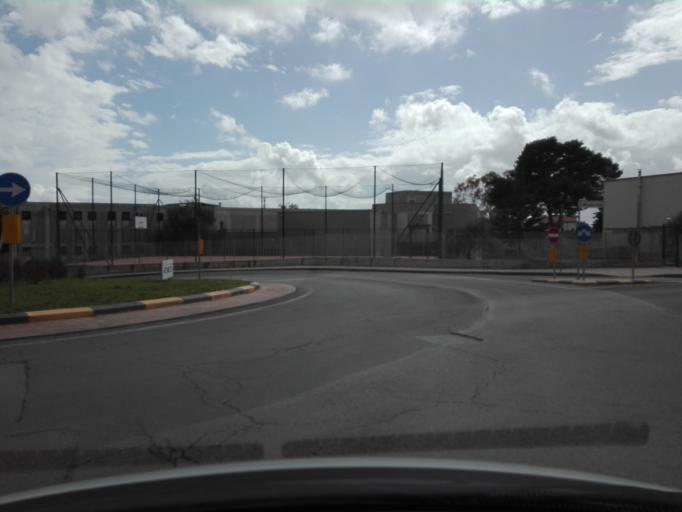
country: IT
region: Sardinia
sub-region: Provincia di Sassari
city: Sassari
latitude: 40.7246
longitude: 8.5758
